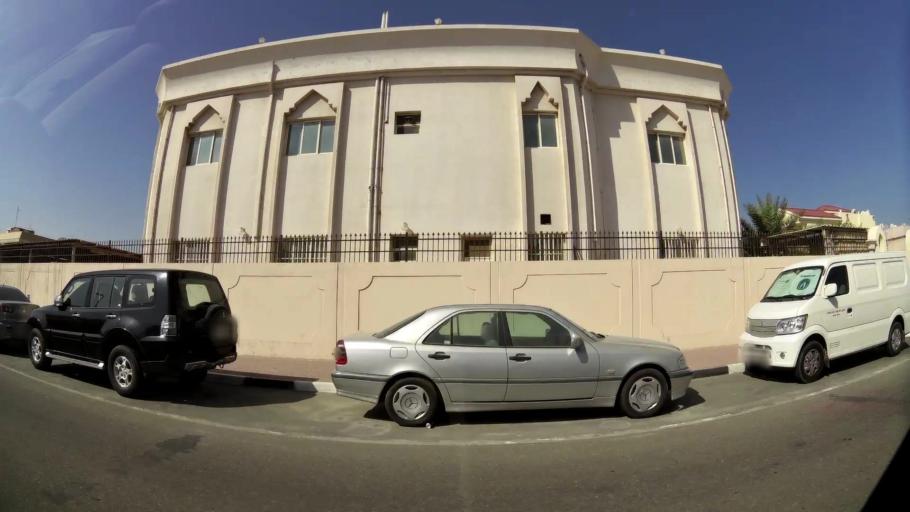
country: AE
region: Ash Shariqah
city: Sharjah
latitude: 25.2470
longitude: 55.2963
